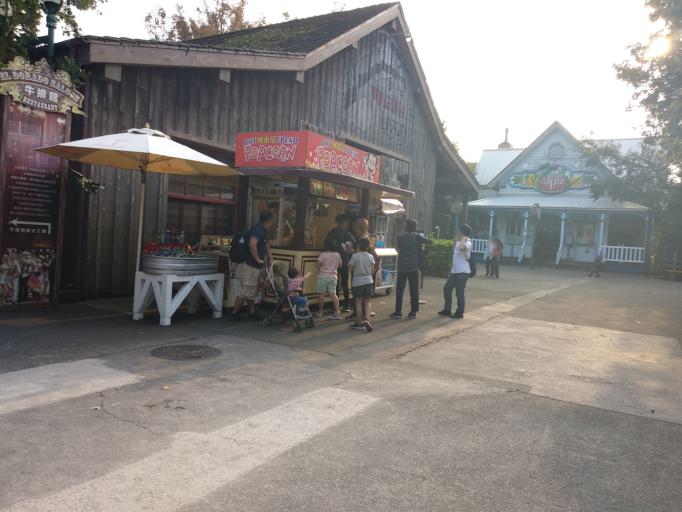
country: TW
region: Taiwan
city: Daxi
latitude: 24.8202
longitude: 121.1826
